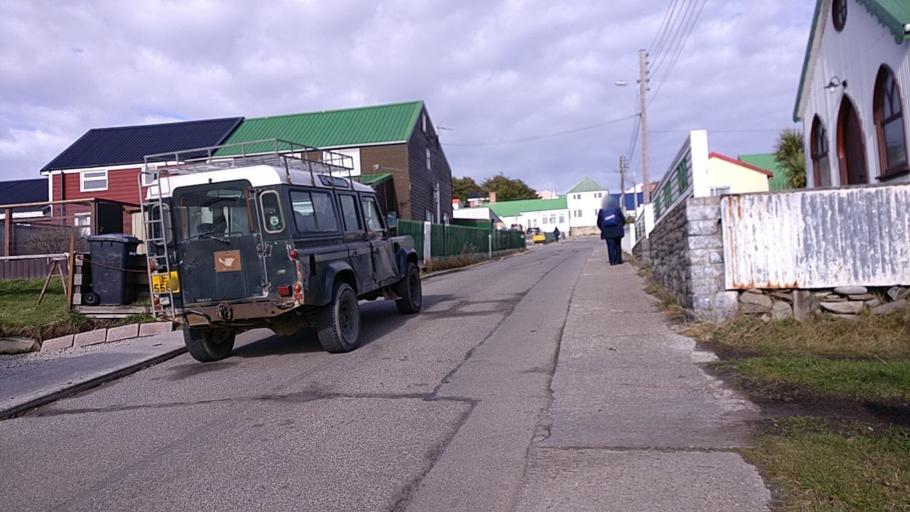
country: FK
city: Stanley
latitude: -51.6920
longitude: -57.8647
